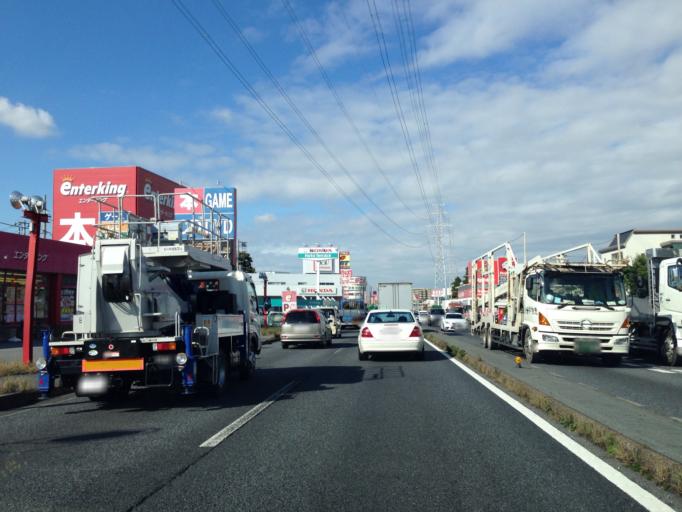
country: JP
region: Chiba
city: Kashiwa
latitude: 35.8848
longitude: 139.9637
